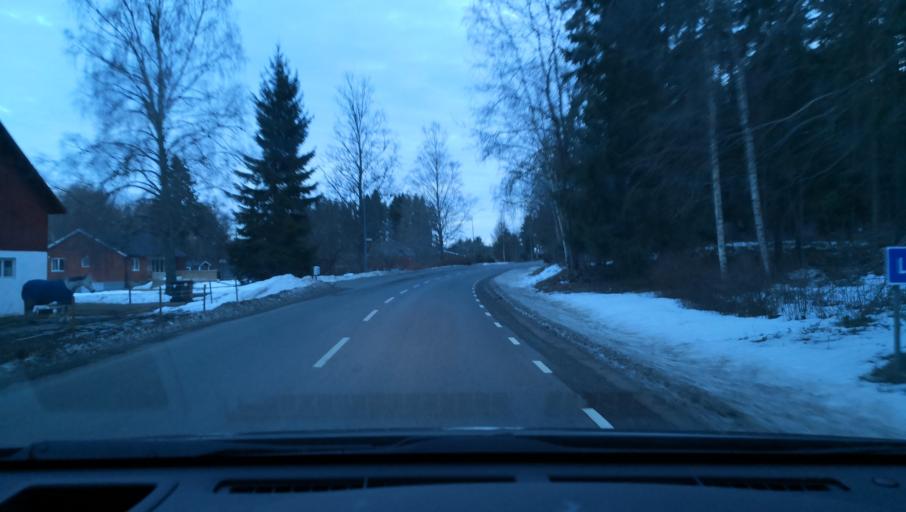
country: SE
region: Uppsala
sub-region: Osthammars Kommun
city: Bjorklinge
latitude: 60.0960
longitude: 17.5602
